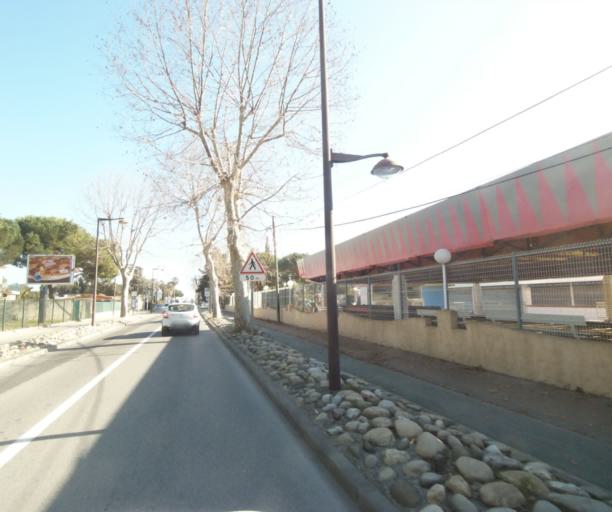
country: FR
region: Provence-Alpes-Cote d'Azur
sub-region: Departement des Alpes-Maritimes
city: Biot
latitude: 43.6132
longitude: 7.1237
